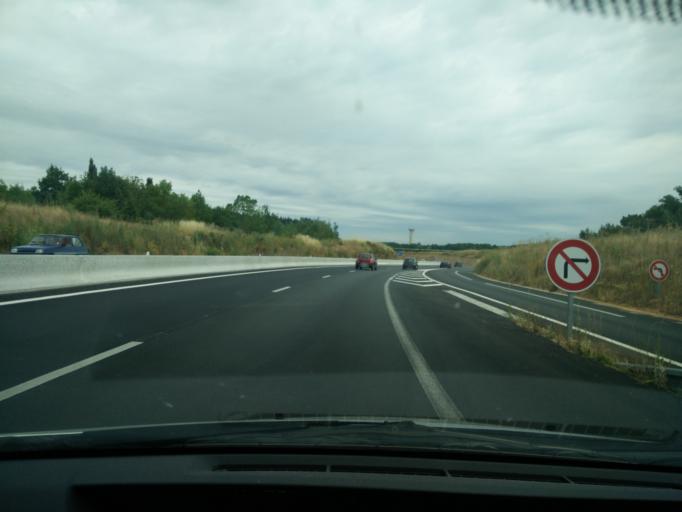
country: FR
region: Pays de la Loire
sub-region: Departement de Maine-et-Loire
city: Saint-Melaine-sur-Aubance
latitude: 47.3934
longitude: -0.5036
